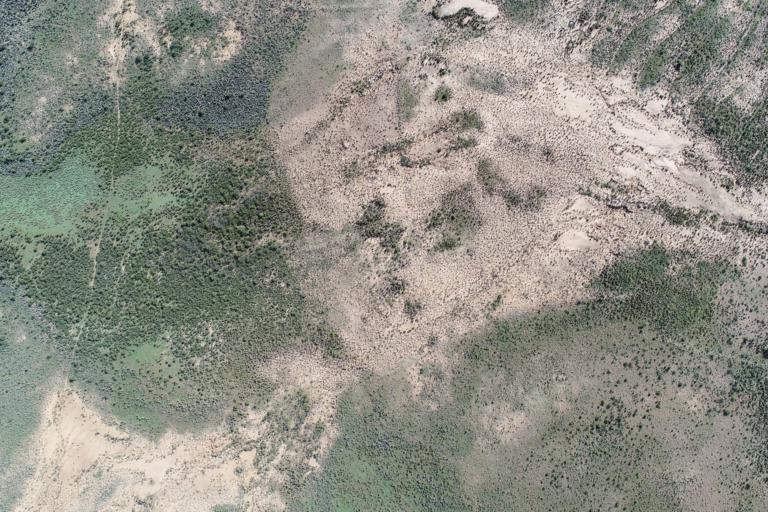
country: BO
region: La Paz
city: Curahuara de Carangas
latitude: -17.3036
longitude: -68.5082
